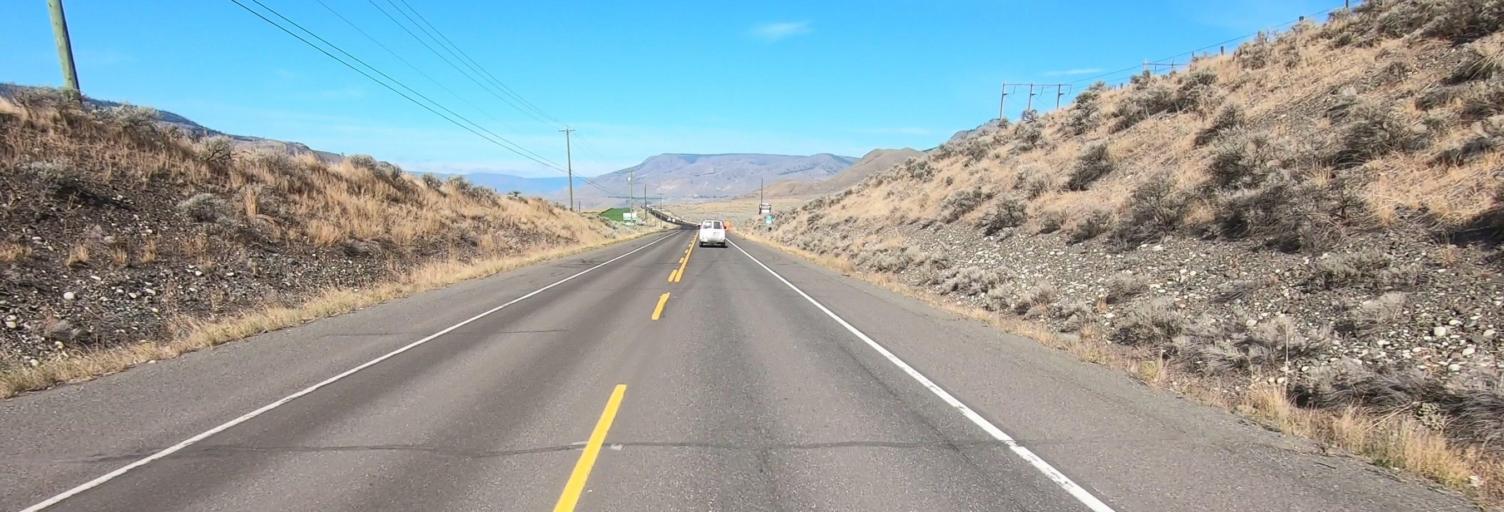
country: CA
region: British Columbia
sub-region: Thompson-Nicola Regional District
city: Ashcroft
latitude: 50.7721
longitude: -121.0259
